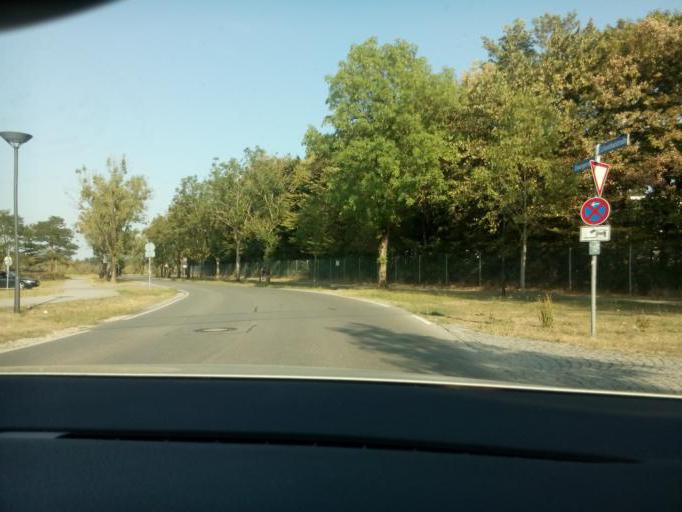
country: DE
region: Bavaria
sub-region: Upper Bavaria
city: Neubiberg
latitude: 48.0827
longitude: 11.6396
